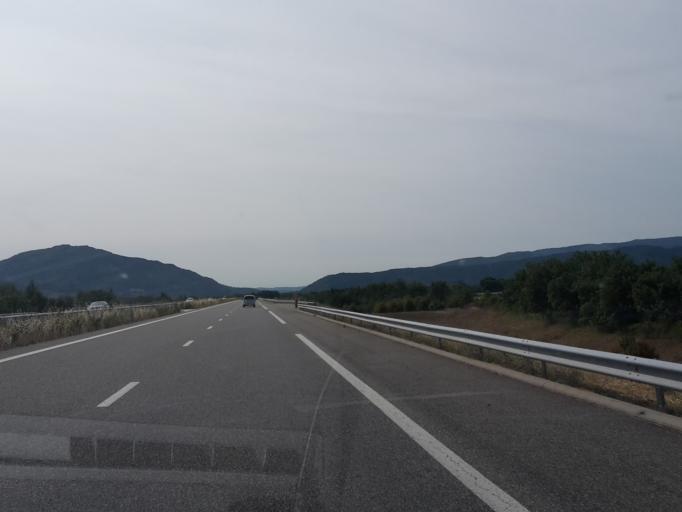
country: FR
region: Provence-Alpes-Cote d'Azur
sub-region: Departement des Alpes-de-Haute-Provence
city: Sisteron
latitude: 44.2704
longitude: 5.9021
